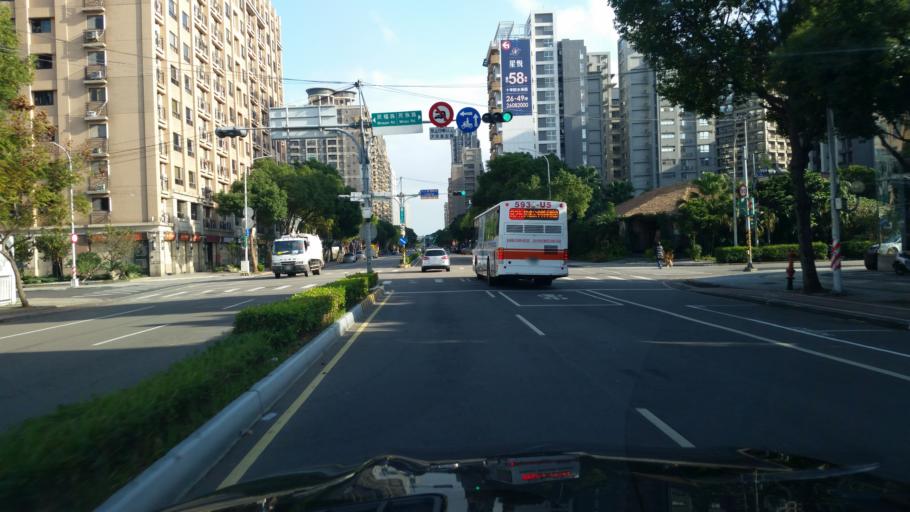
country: TW
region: Taiwan
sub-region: Taoyuan
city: Taoyuan
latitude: 25.0798
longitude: 121.3705
